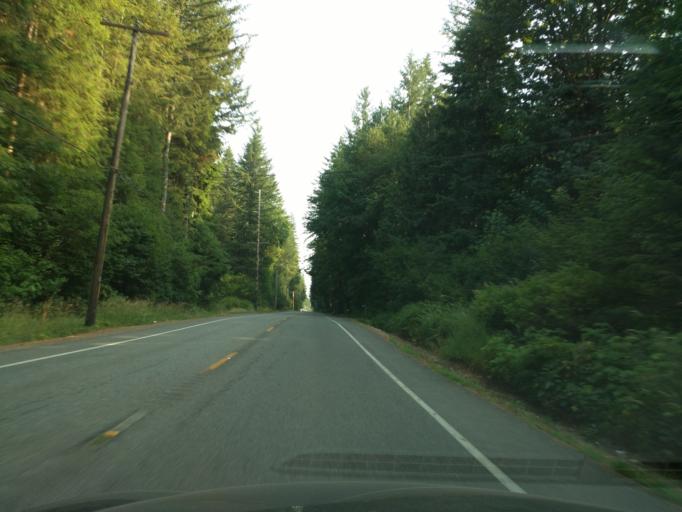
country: US
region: Washington
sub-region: Whatcom County
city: Peaceful Valley
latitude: 48.9306
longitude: -122.1436
